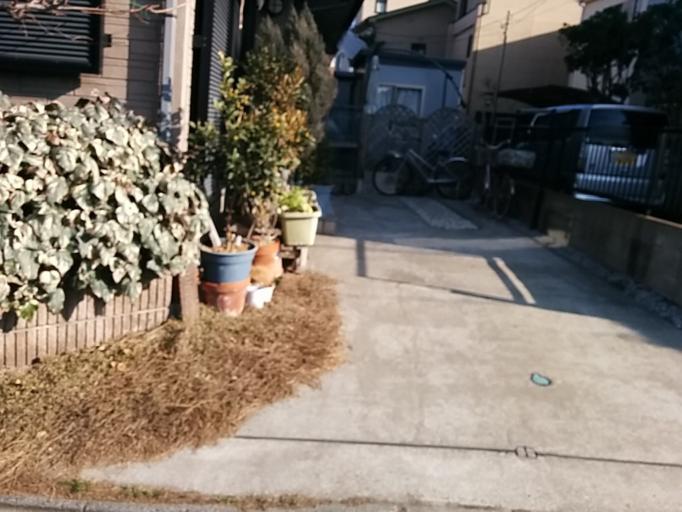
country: JP
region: Saitama
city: Kawagoe
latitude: 35.9209
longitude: 139.4774
